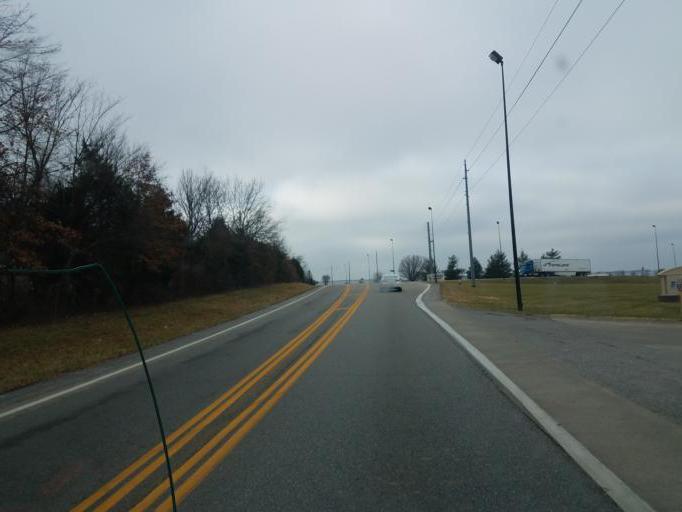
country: US
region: Missouri
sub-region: Greene County
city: Strafford
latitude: 37.2457
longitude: -93.1929
